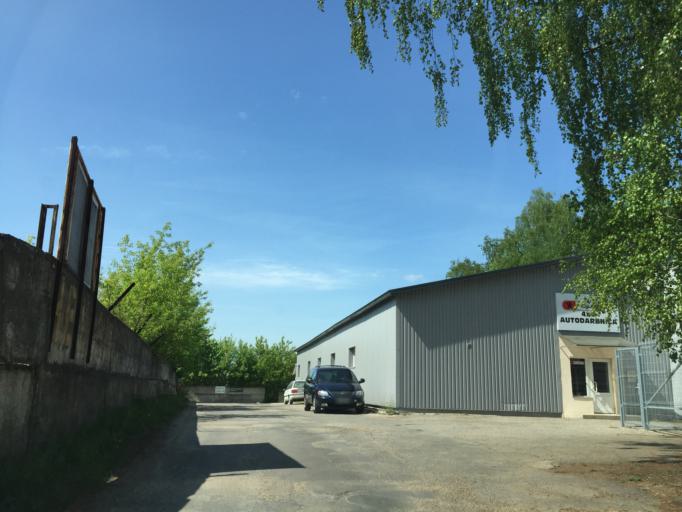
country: LV
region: Riga
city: Bergi
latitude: 56.9984
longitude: 24.2679
